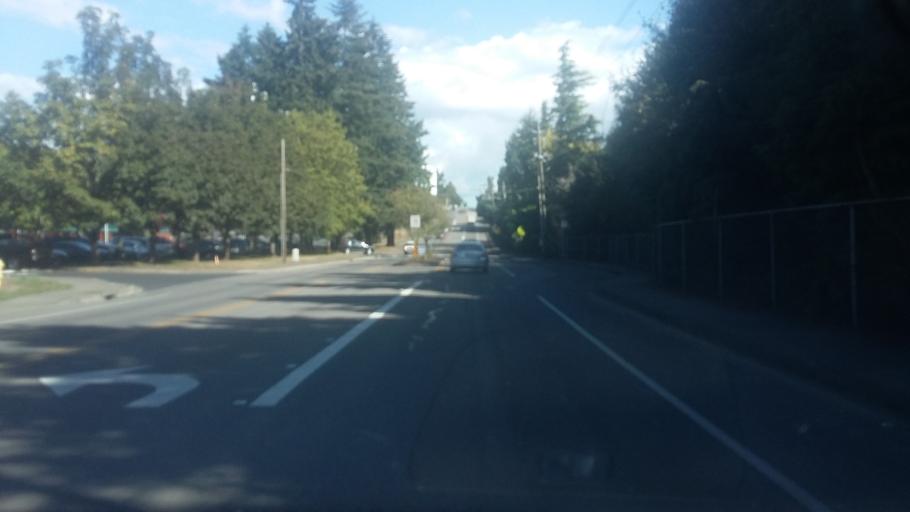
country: US
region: Washington
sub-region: Clark County
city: Salmon Creek
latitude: 45.6931
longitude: -122.6410
